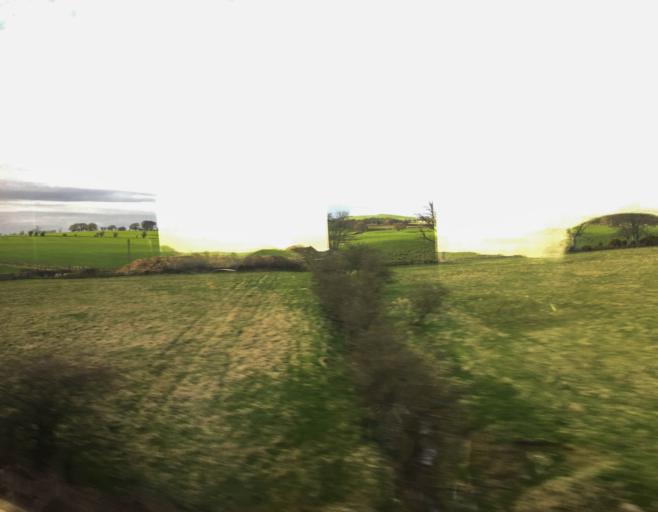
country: GB
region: Scotland
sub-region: Dumfries and Galloway
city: Lockerbie
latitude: 55.1038
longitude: -3.3394
